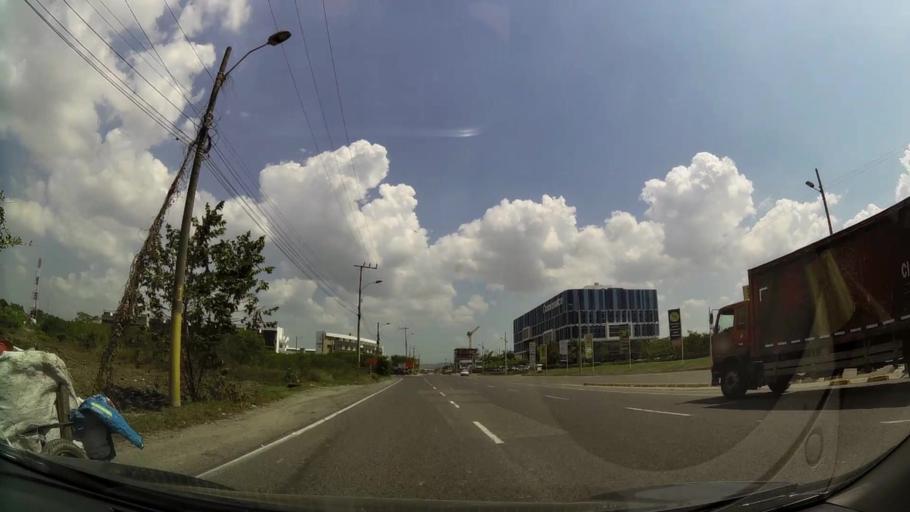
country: CO
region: Bolivar
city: Cartagena
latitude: 10.3424
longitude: -75.4963
